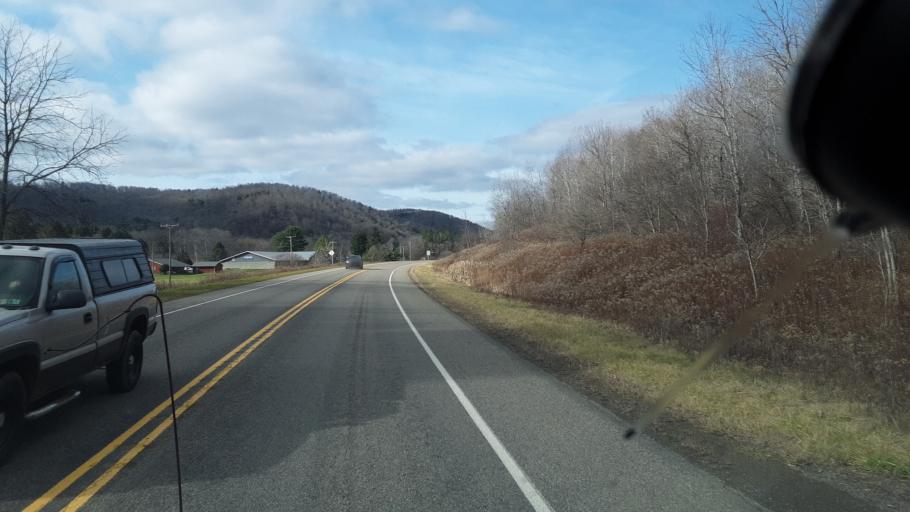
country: US
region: Pennsylvania
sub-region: Potter County
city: Galeton
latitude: 41.7775
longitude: -77.7219
